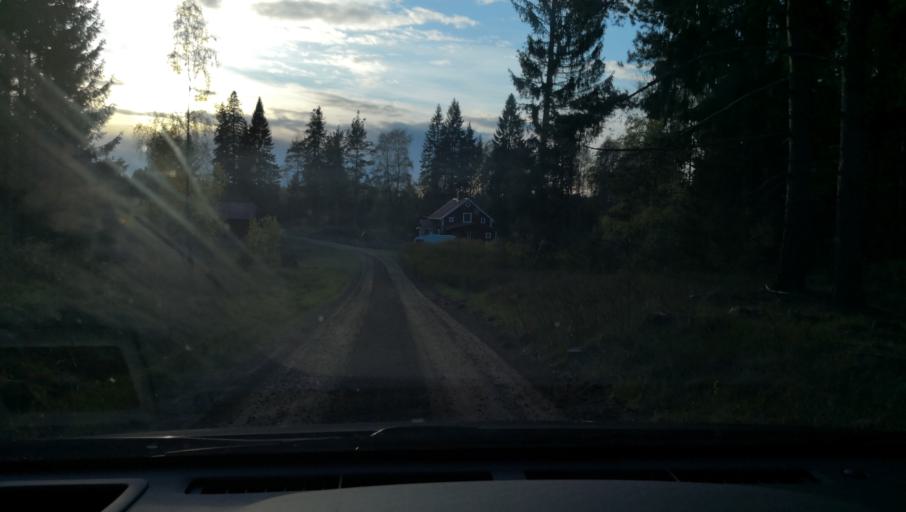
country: SE
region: OErebro
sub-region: Askersunds Kommun
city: Asbro
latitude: 58.8867
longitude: 15.1237
